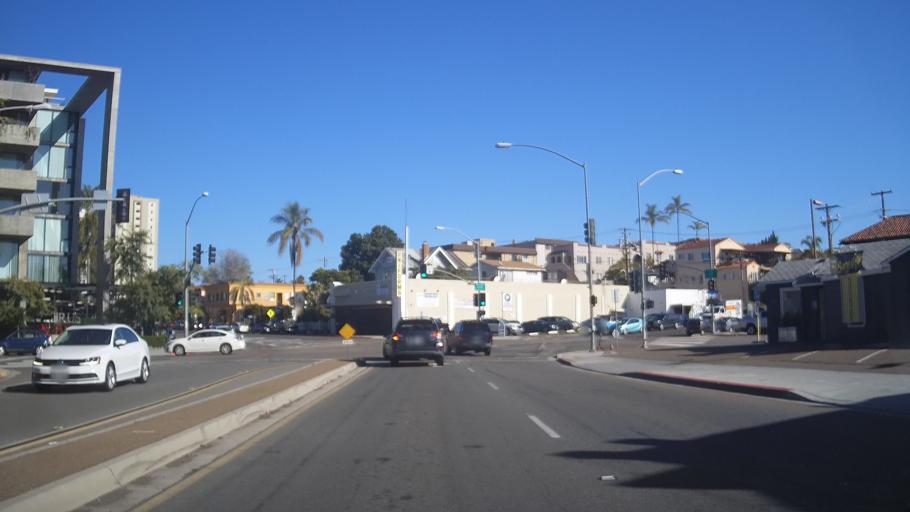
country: US
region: California
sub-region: San Diego County
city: San Diego
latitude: 32.7458
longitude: -117.1467
